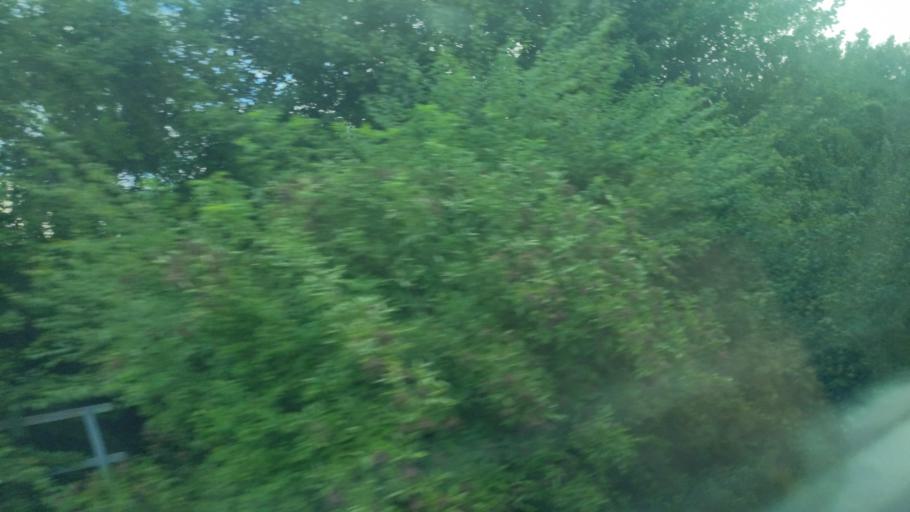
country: CZ
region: Central Bohemia
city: Cesky Brod
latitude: 50.0784
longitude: 14.8013
